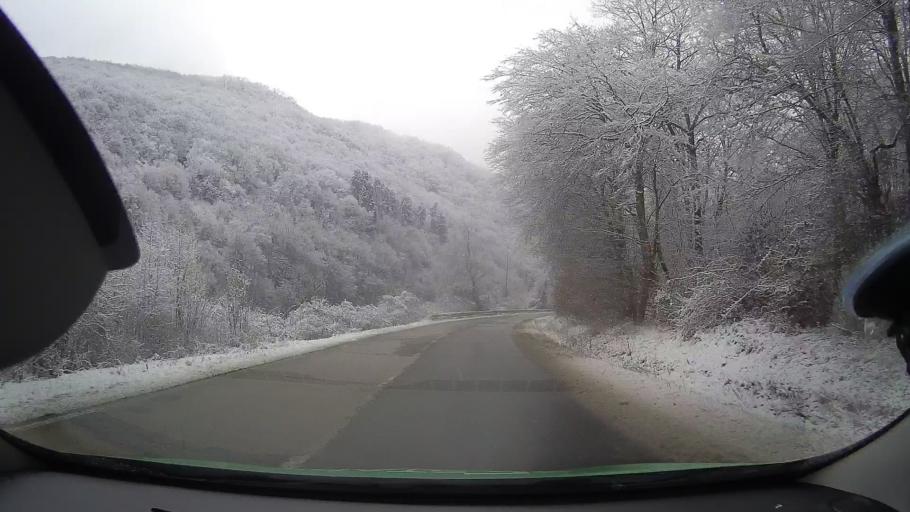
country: RO
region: Cluj
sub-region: Comuna Moldovenesti
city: Moldovenesti
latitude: 46.5061
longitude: 23.6387
